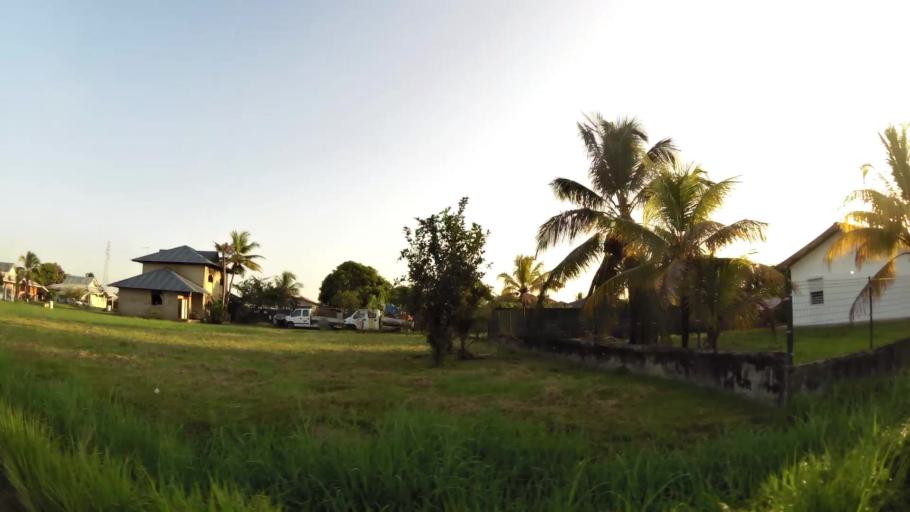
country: GF
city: Macouria
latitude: 5.0083
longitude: -52.4691
